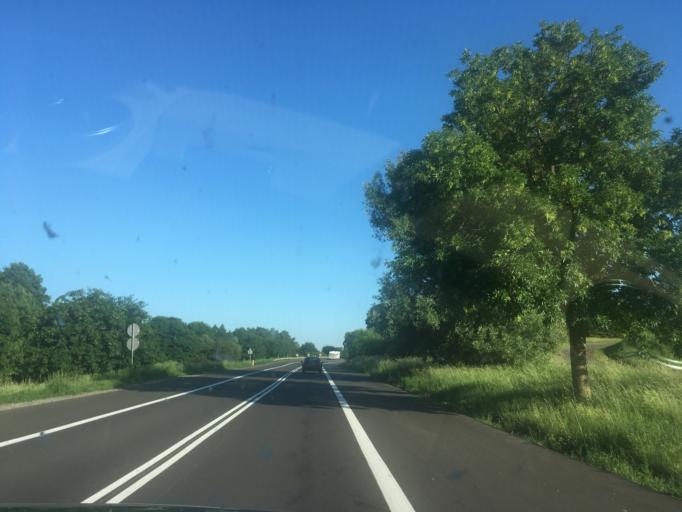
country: PL
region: Warmian-Masurian Voivodeship
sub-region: Powiat ostrodzki
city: Ostroda
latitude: 53.6701
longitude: 20.0359
